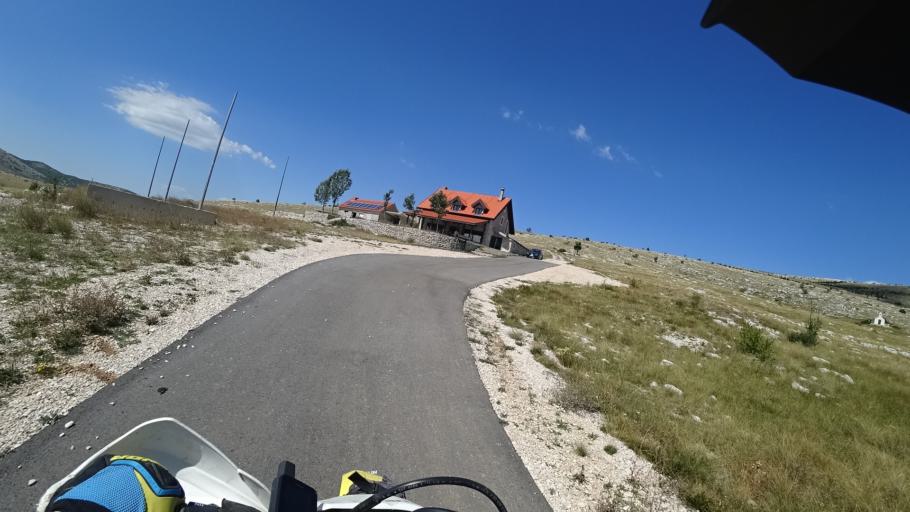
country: HR
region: Splitsko-Dalmatinska
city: Hrvace
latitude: 43.8588
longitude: 16.6396
